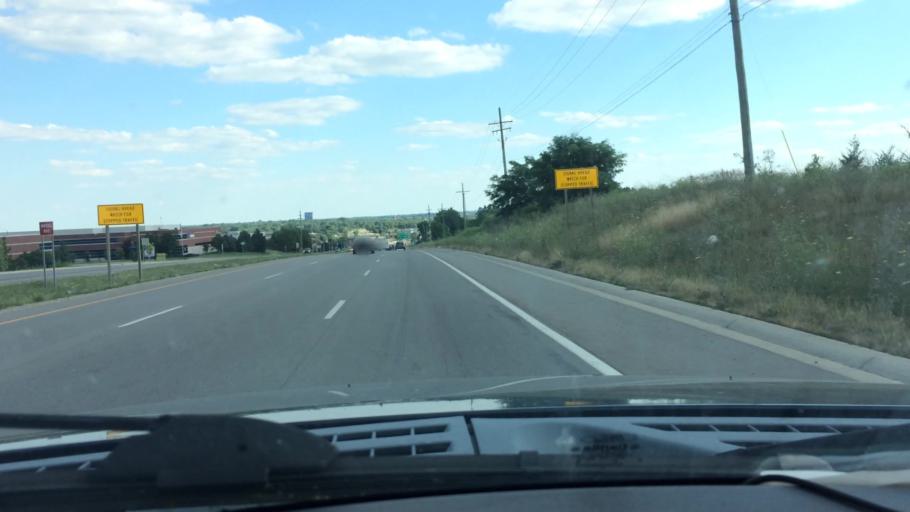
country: US
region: Michigan
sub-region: Oakland County
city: Auburn Hills
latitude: 42.7057
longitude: -83.2427
